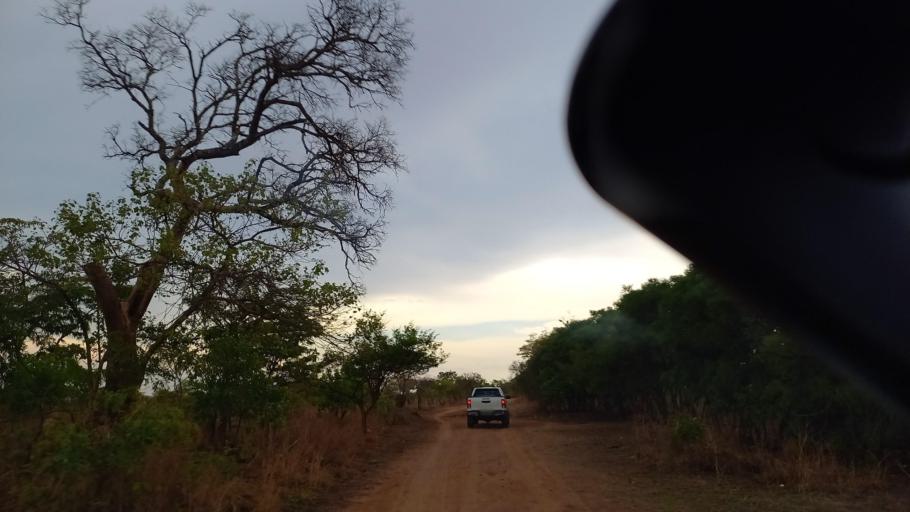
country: ZM
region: Lusaka
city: Kafue
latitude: -16.0322
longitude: 28.3047
